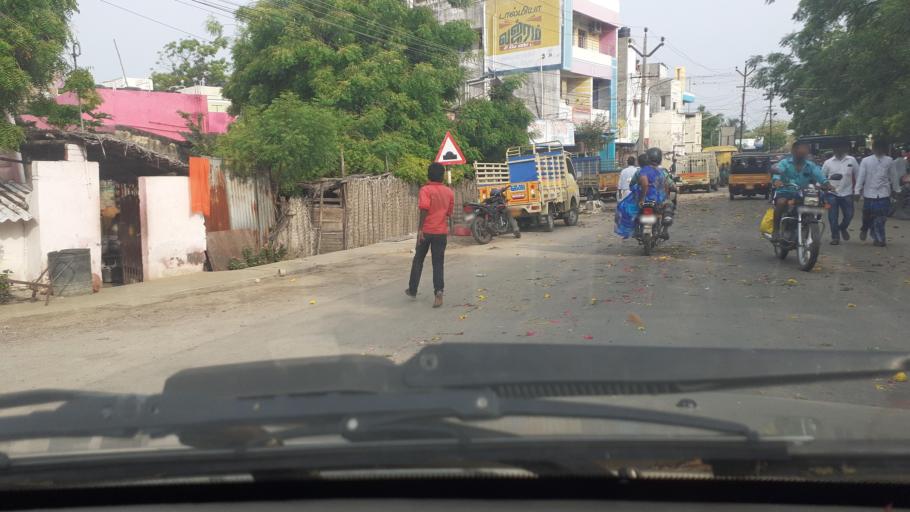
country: IN
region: Tamil Nadu
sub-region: Thoothukkudi
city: Korampallam
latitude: 8.7905
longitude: 78.1147
